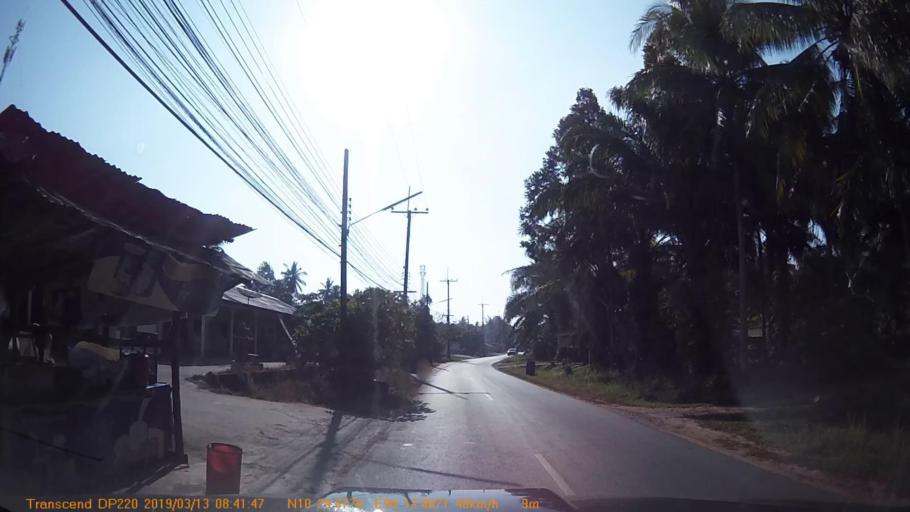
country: TH
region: Chumphon
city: Chumphon
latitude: 10.4979
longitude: 99.2149
